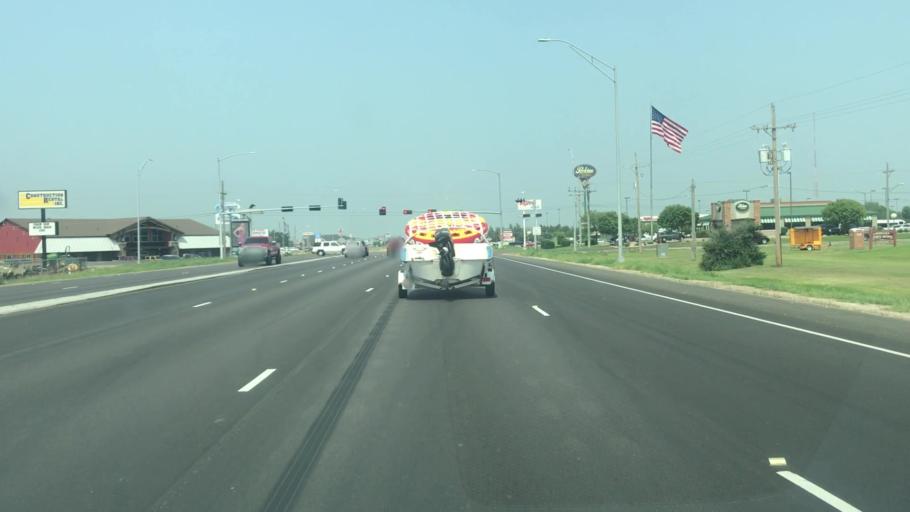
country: US
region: Nebraska
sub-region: Hall County
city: Grand Island
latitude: 40.9160
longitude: -98.3832
